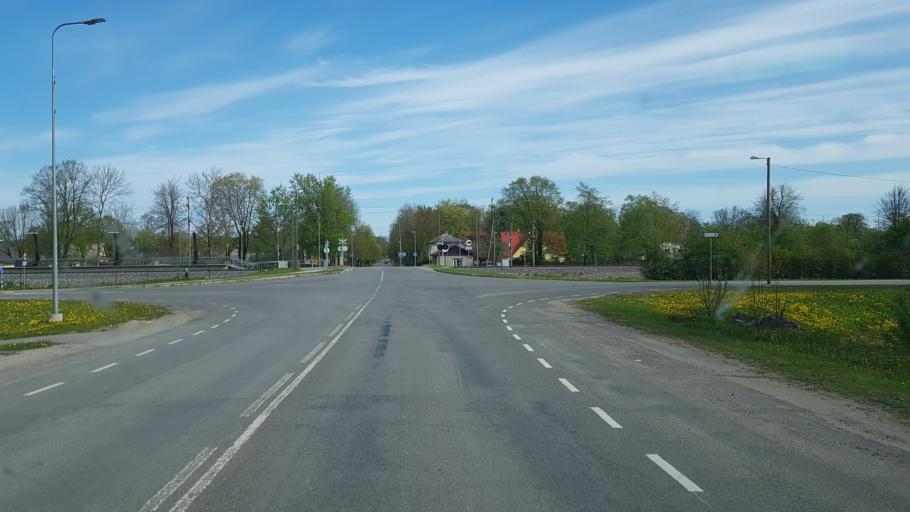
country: EE
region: Ida-Virumaa
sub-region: Kivioli linn
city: Kivioli
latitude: 59.3523
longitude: 26.9670
